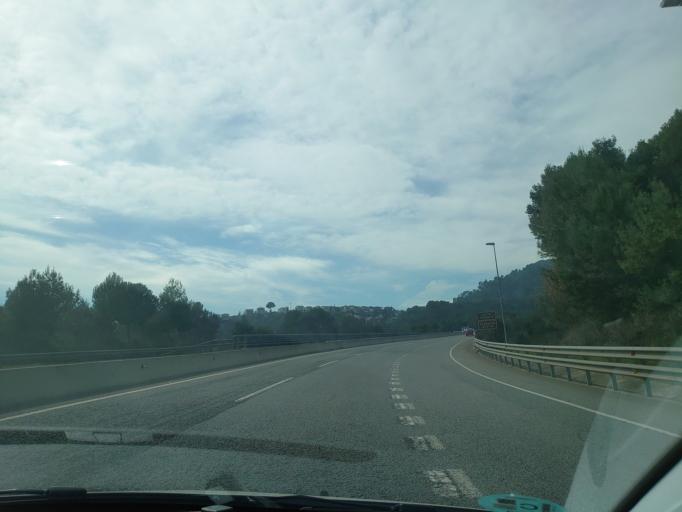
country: ES
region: Catalonia
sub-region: Provincia de Barcelona
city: Cervello
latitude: 41.3962
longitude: 1.9697
